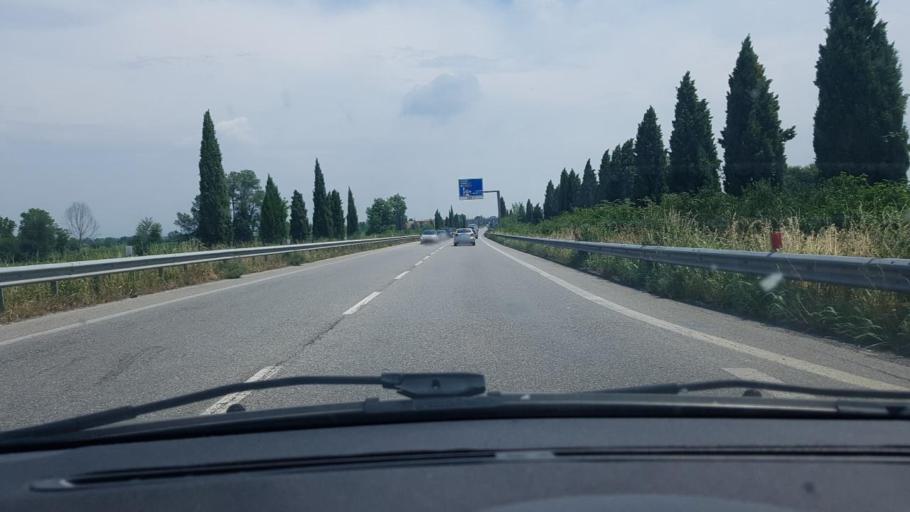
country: IT
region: Lombardy
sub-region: Provincia di Brescia
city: San Martino della Battaglia
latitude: 45.4447
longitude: 10.6084
